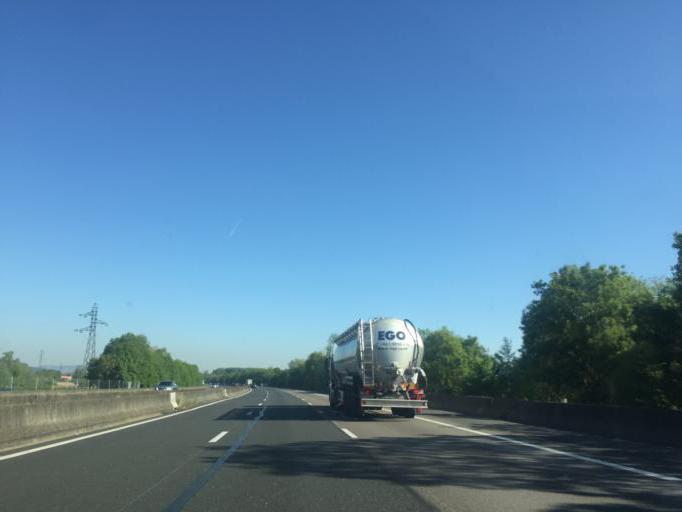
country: FR
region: Bourgogne
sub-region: Departement de Saone-et-Loire
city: Creches-sur-Saone
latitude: 46.2492
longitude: 4.7989
